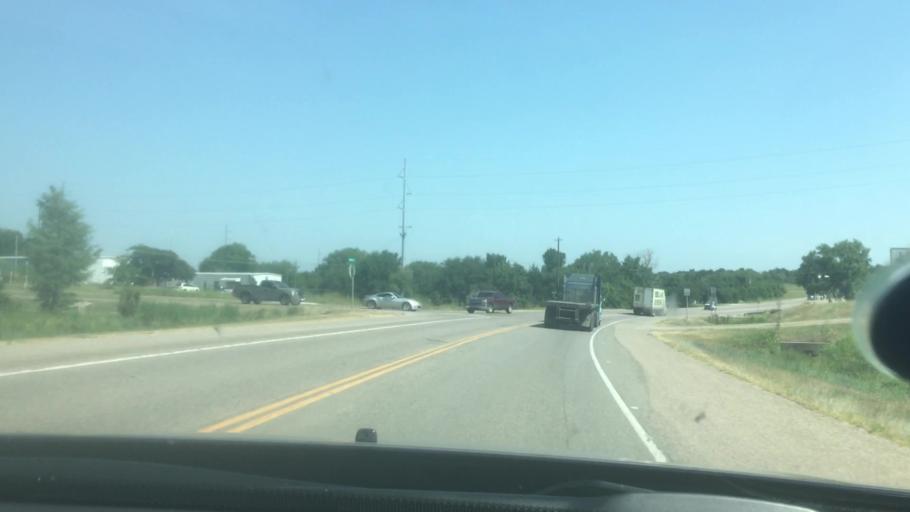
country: US
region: Oklahoma
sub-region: Pontotoc County
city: Ada
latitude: 34.7594
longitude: -96.7036
